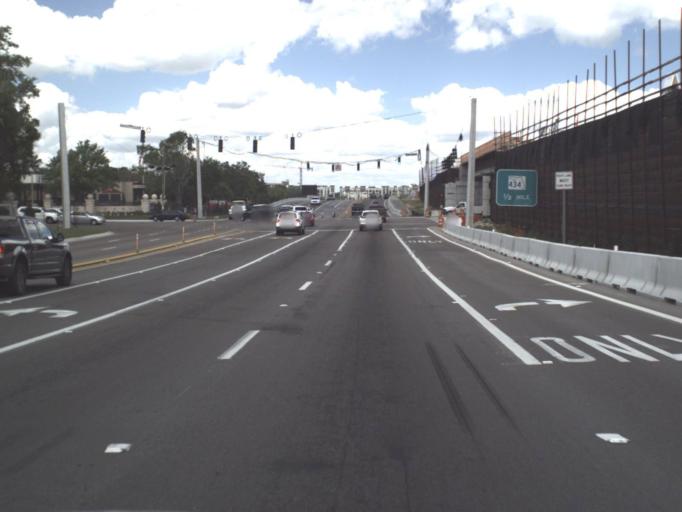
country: US
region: Florida
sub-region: Orange County
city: Eatonville
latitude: 28.6353
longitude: -81.4021
